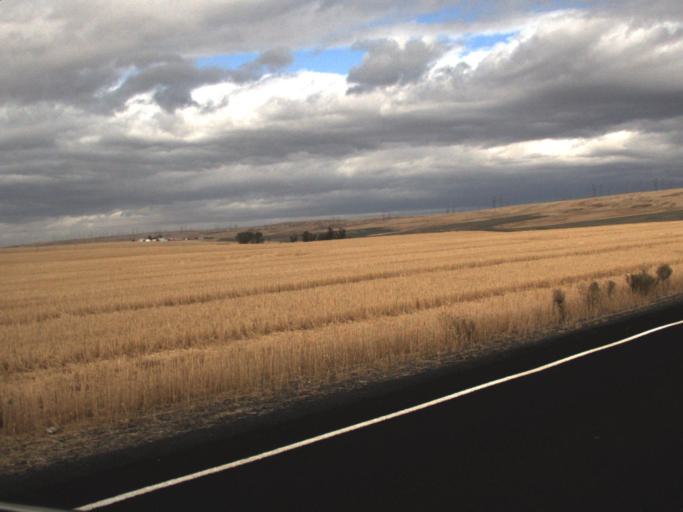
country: US
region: Washington
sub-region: Okanogan County
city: Coulee Dam
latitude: 47.8254
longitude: -118.7218
